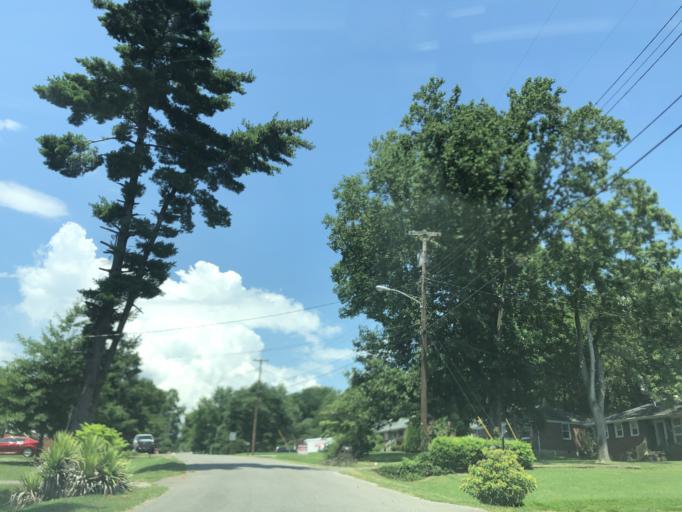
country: US
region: Tennessee
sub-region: Davidson County
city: Lakewood
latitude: 36.1545
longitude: -86.6549
